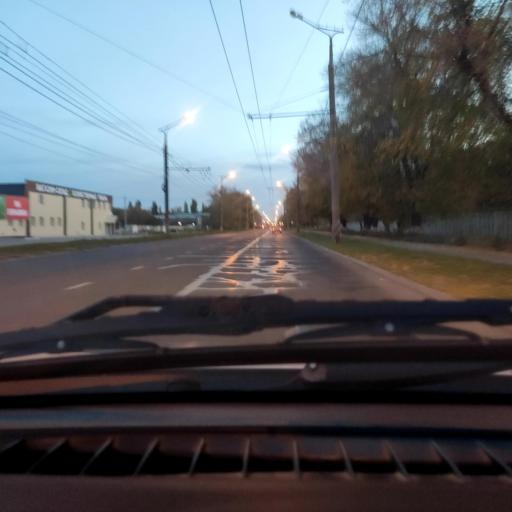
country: RU
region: Samara
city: Tol'yatti
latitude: 53.5254
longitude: 49.4351
